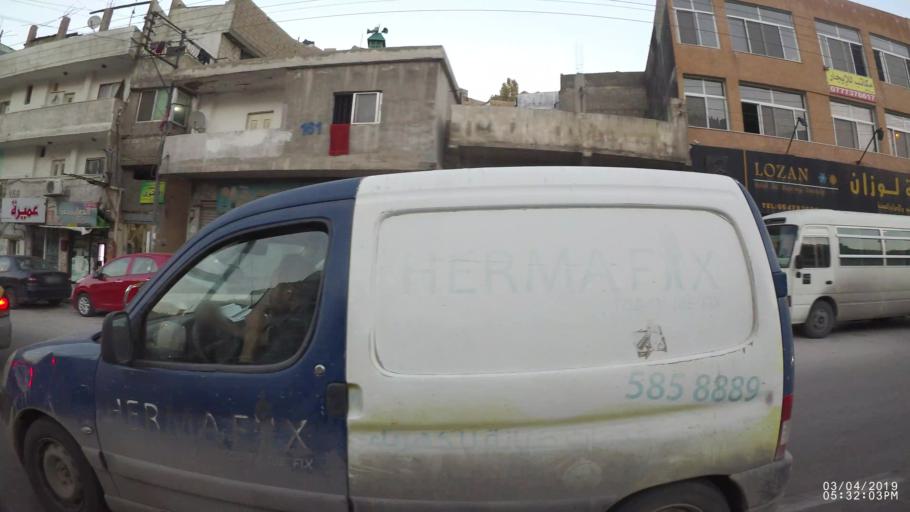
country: JO
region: Amman
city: Amman
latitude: 31.9379
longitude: 35.9239
